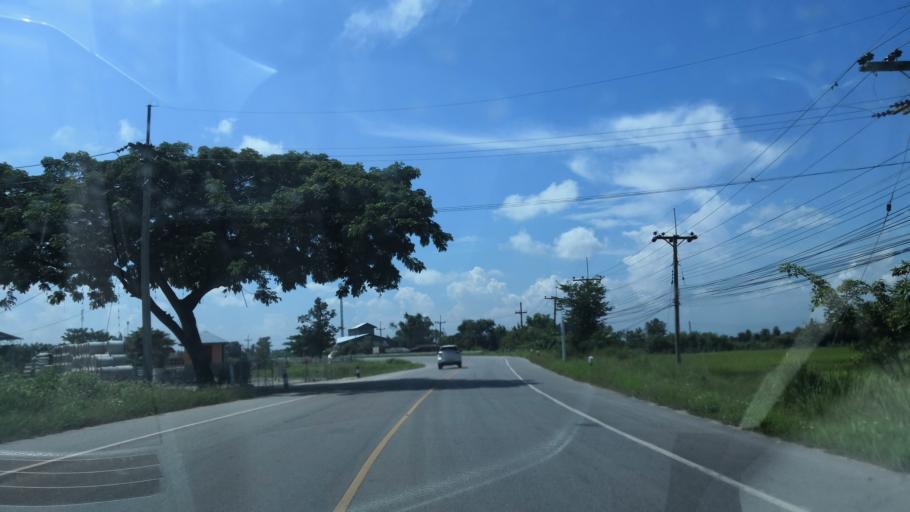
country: TH
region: Chiang Rai
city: Wiang Chiang Rung
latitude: 19.9720
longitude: 100.0148
